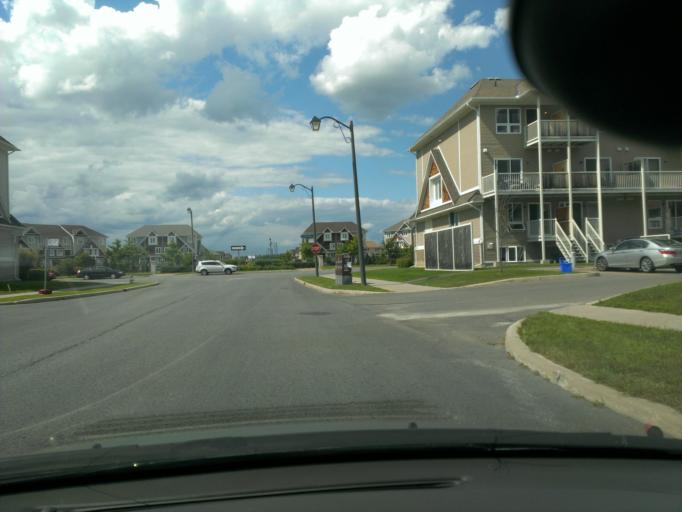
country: CA
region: Ontario
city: Clarence-Rockland
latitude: 45.4485
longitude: -75.4754
